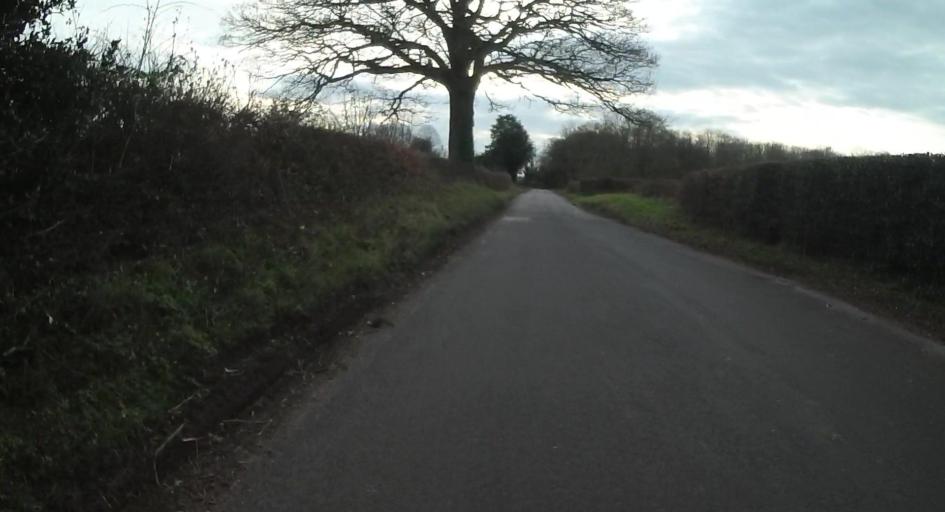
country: GB
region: England
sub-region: West Berkshire
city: Theale
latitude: 51.4085
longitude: -1.0725
